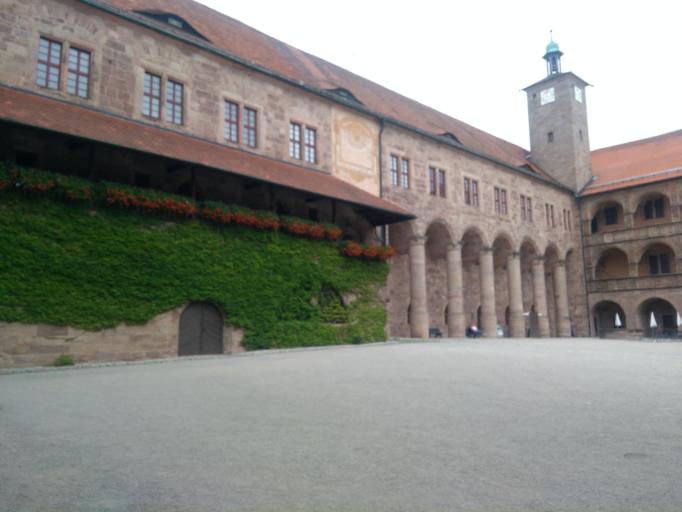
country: DE
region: Bavaria
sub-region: Upper Franconia
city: Kulmbach
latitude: 50.1079
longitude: 11.4634
